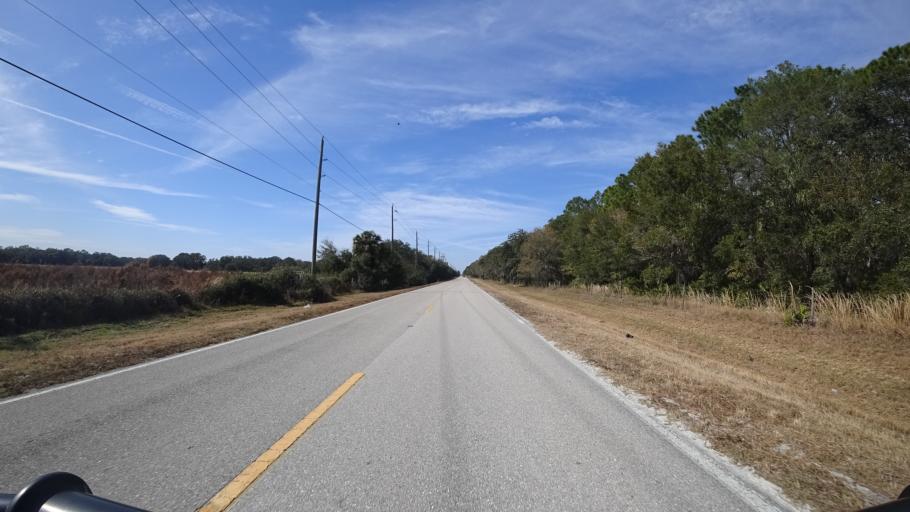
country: US
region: Florida
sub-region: Manatee County
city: Ellenton
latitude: 27.5136
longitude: -82.3806
